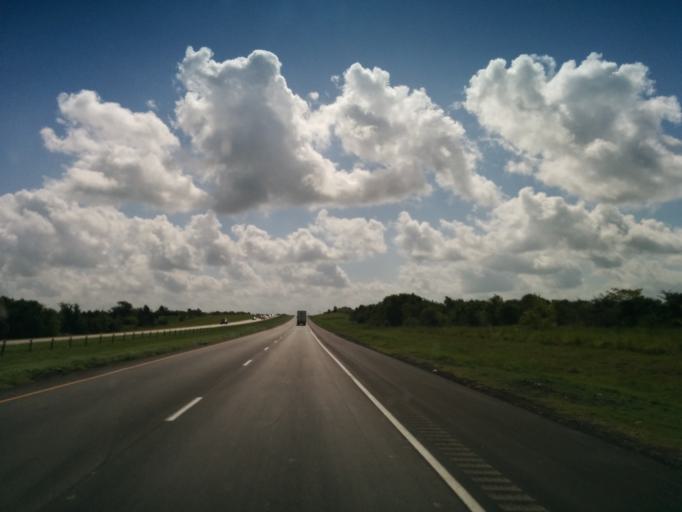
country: US
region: Texas
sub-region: Colorado County
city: Weimar
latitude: 29.6886
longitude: -96.8198
